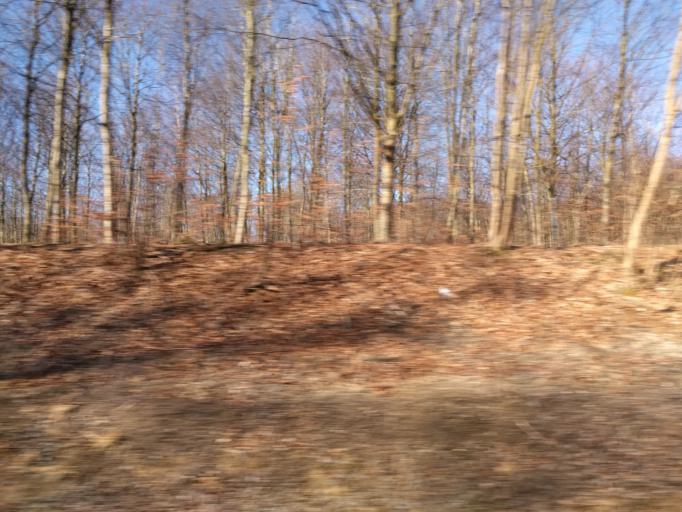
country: DK
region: Capital Region
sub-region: Rudersdal Kommune
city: Trorod
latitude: 55.8293
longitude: 12.5698
